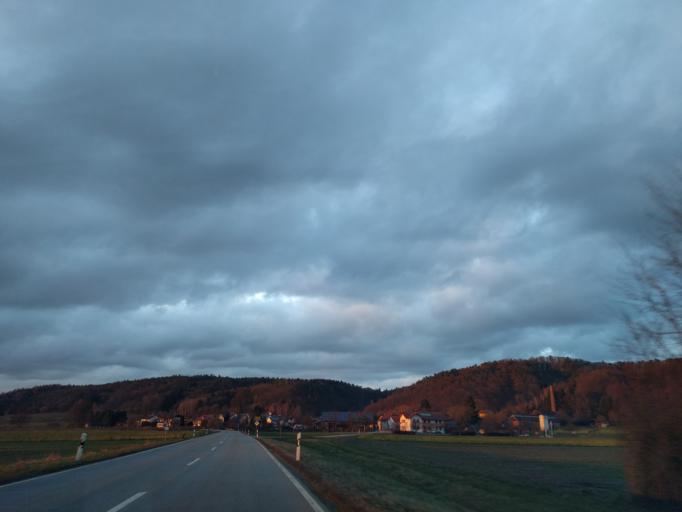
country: DE
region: Bavaria
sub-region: Lower Bavaria
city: Winzer
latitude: 48.7105
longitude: 13.1057
